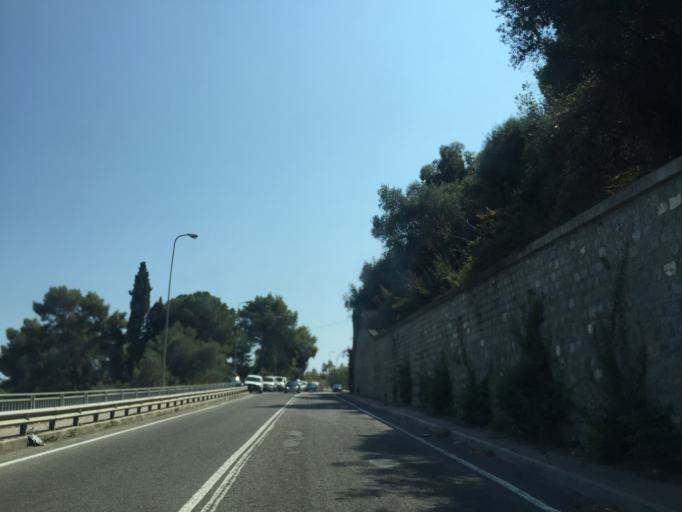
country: IT
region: Liguria
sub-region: Provincia di Imperia
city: Ventimiglia
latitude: 43.7876
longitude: 7.5582
